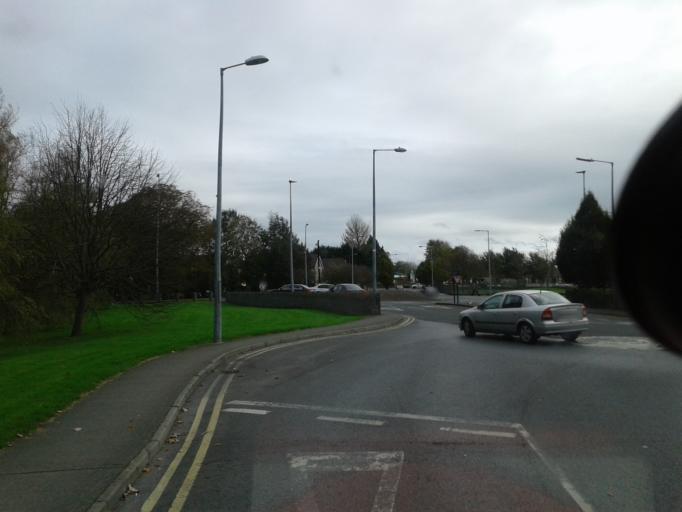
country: IE
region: Munster
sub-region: An Clar
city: Ennis
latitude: 52.8439
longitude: -8.9784
